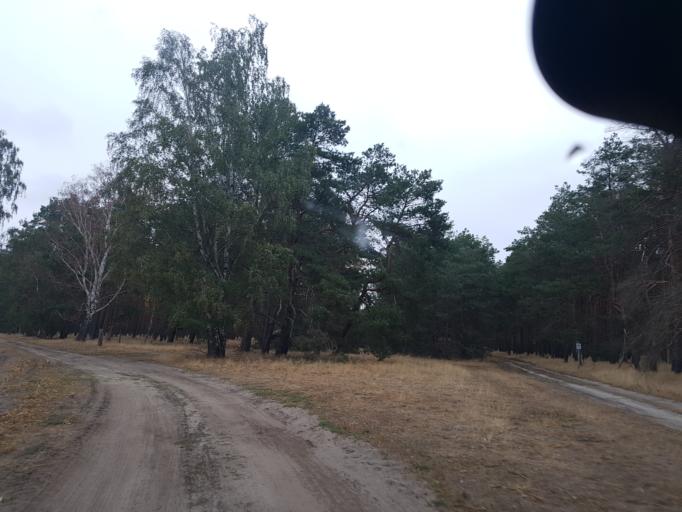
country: DE
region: Brandenburg
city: Schilda
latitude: 51.6418
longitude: 13.3300
